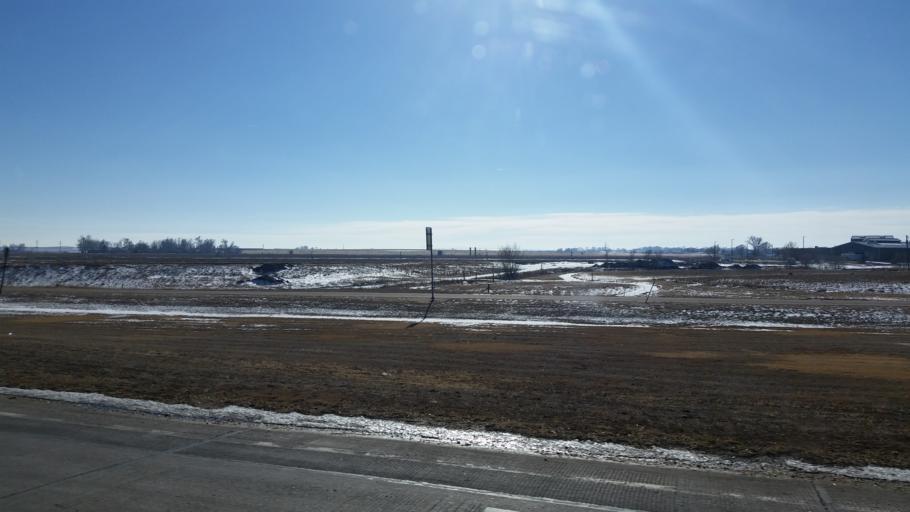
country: US
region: Colorado
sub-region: Weld County
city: Kersey
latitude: 40.3922
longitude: -104.5495
